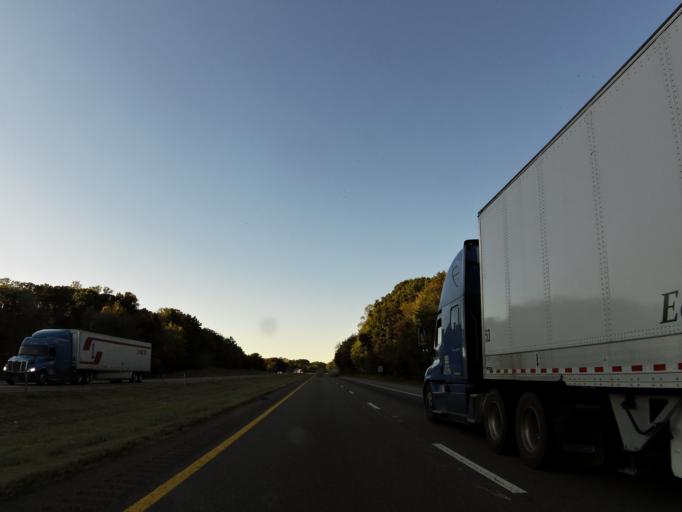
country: US
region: Tennessee
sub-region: Knox County
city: Knoxville
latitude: 36.0595
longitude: -84.0067
